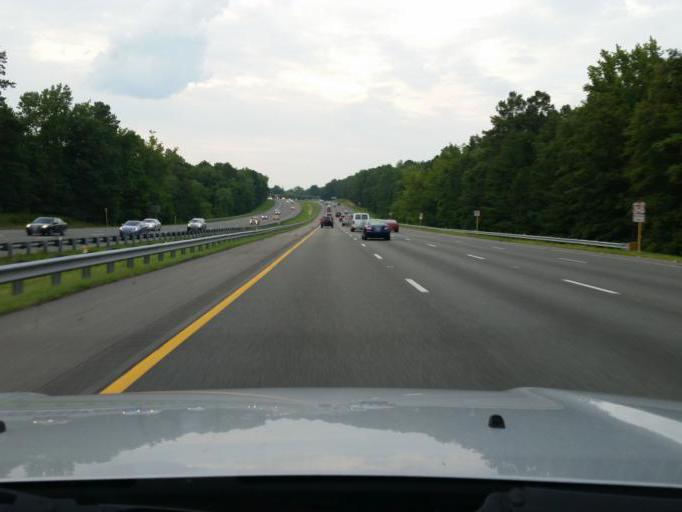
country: US
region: Virginia
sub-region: Caroline County
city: Bowling Green
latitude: 37.9850
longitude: -77.4926
